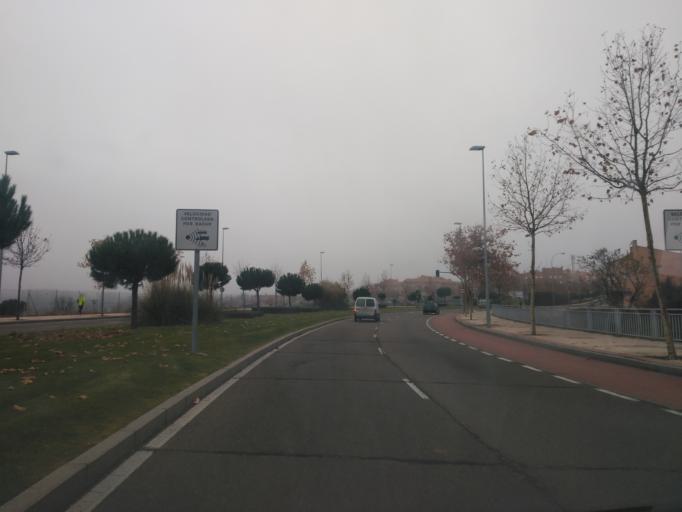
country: ES
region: Castille and Leon
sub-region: Provincia de Salamanca
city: Salamanca
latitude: 40.9660
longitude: -5.6439
